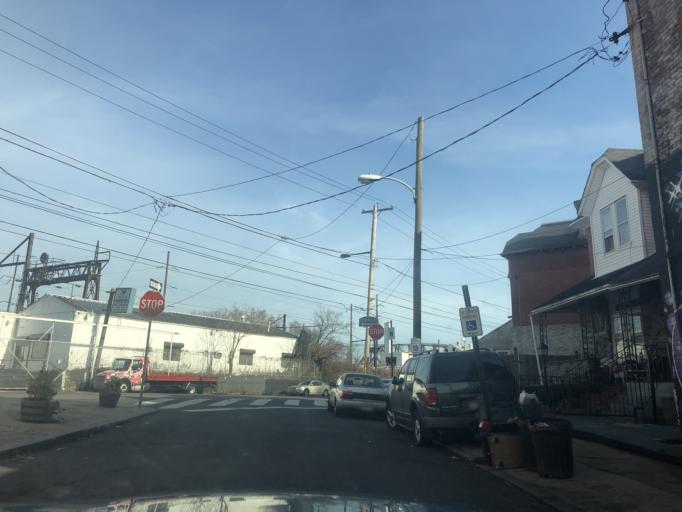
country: US
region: Pennsylvania
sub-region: Delaware County
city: Millbourne
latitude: 39.9791
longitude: -75.2313
